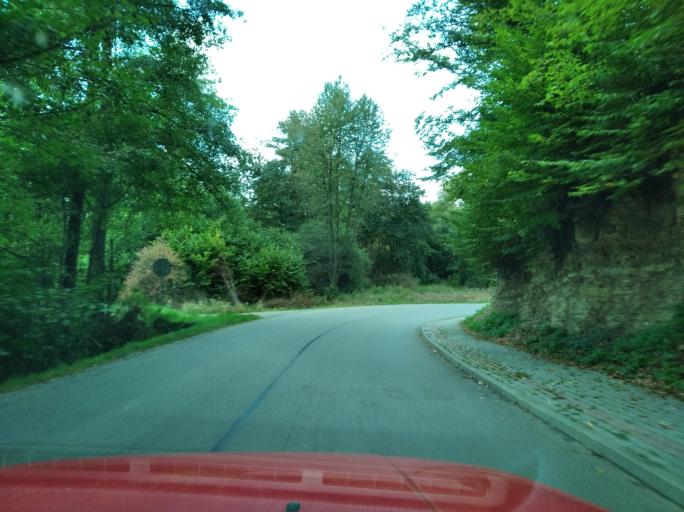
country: PL
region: Subcarpathian Voivodeship
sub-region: Powiat rzeszowski
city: Tyczyn
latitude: 49.9342
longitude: 22.0195
